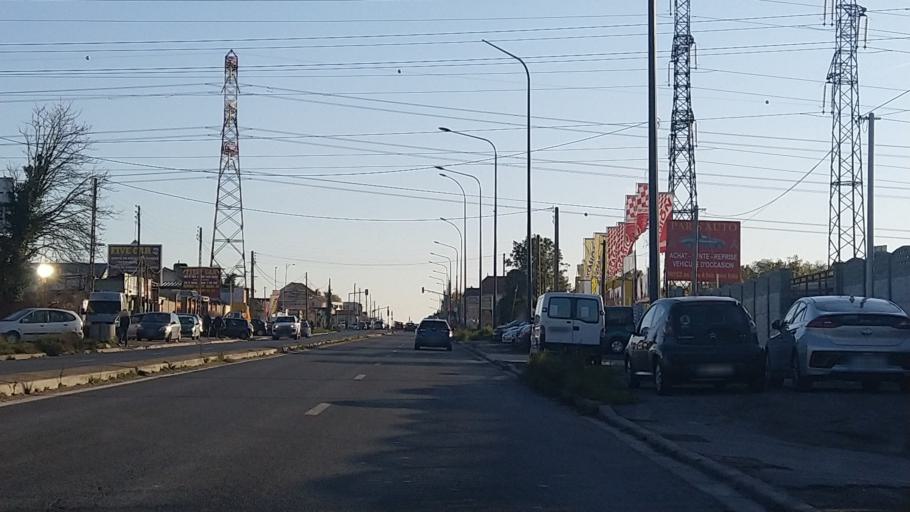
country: FR
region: Ile-de-France
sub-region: Departement de Seine-Saint-Denis
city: Pierrefitte-sur-Seine
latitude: 48.9812
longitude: 2.3630
